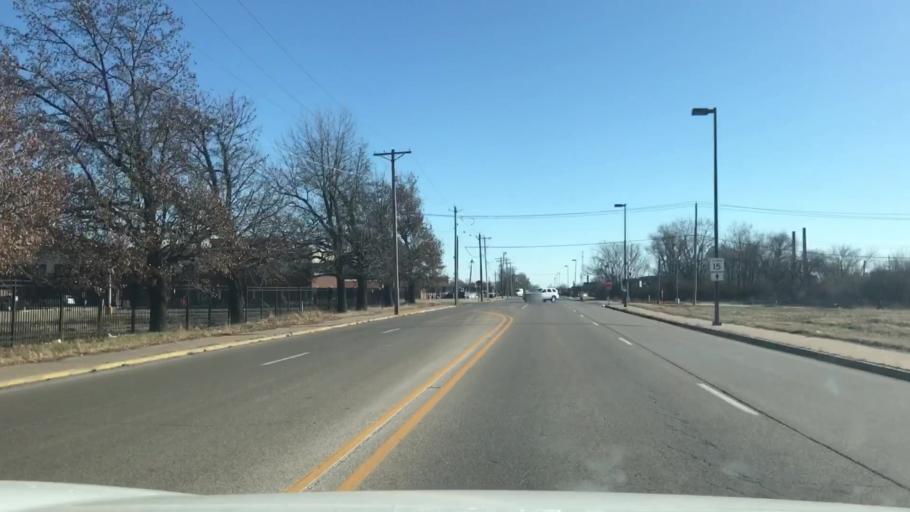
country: US
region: Illinois
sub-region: Saint Clair County
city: East Saint Louis
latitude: 38.6226
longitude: -90.1589
